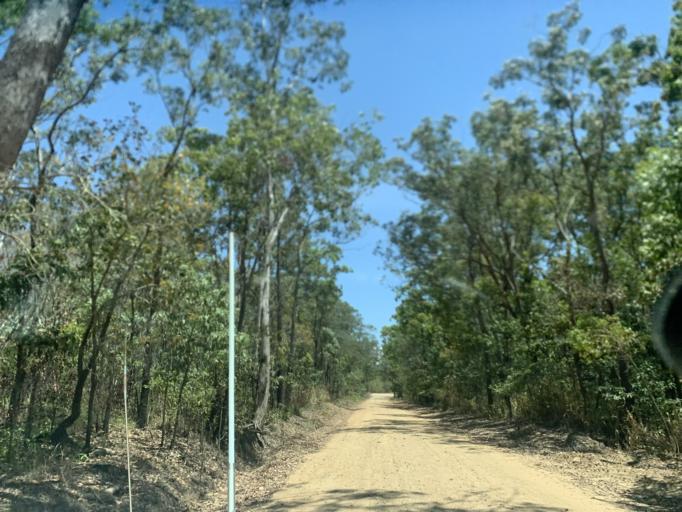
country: AU
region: Queensland
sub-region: Tablelands
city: Kuranda
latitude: -16.9209
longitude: 145.5908
